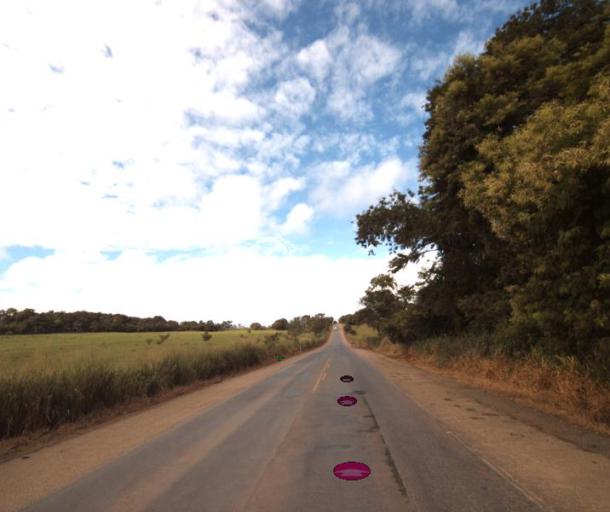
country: BR
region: Goias
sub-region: Uruacu
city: Uruacu
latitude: -14.7393
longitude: -49.2451
